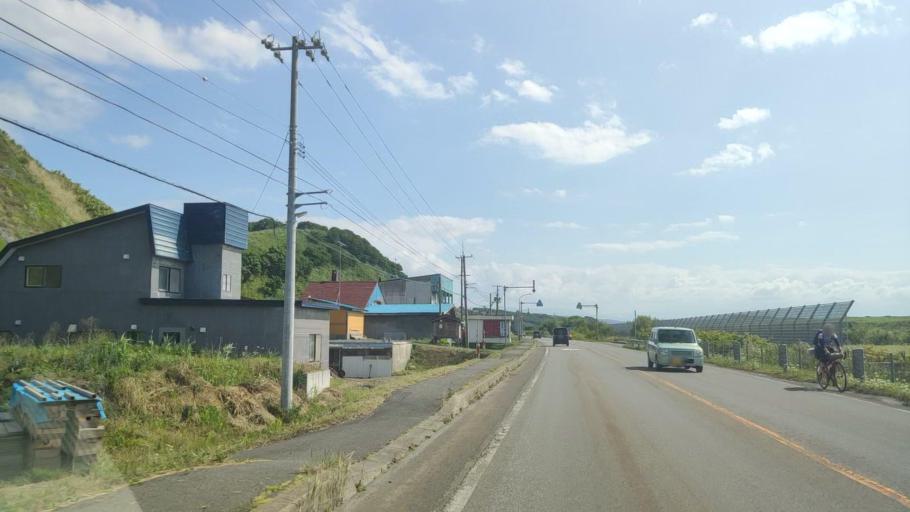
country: JP
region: Hokkaido
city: Rumoi
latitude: 43.9760
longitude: 141.6465
